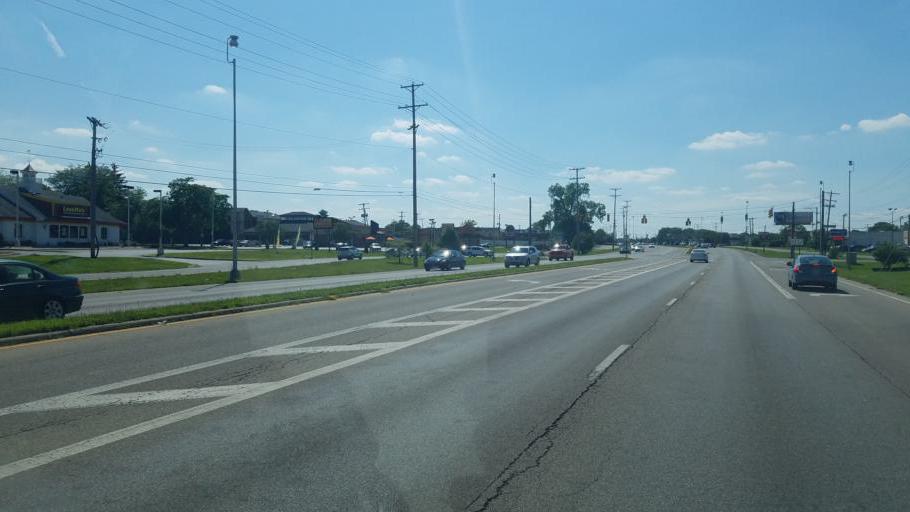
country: US
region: Ohio
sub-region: Franklin County
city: Minerva Park
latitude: 40.0860
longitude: -82.9553
